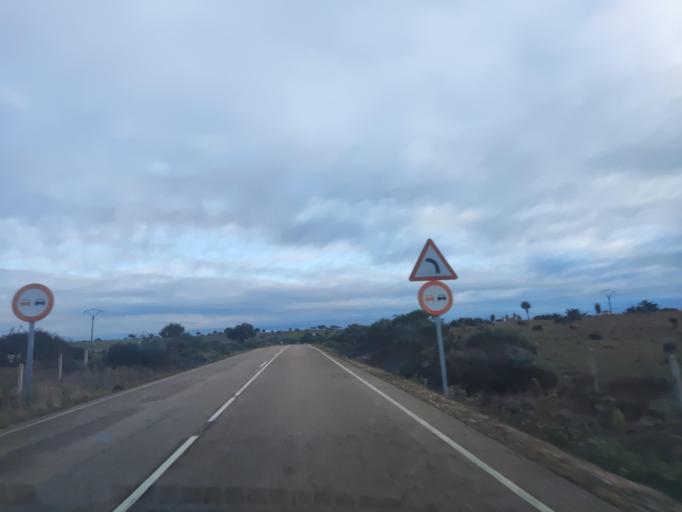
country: ES
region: Castille and Leon
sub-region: Provincia de Salamanca
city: Castillejo de Martin Viejo
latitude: 40.7565
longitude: -6.6419
